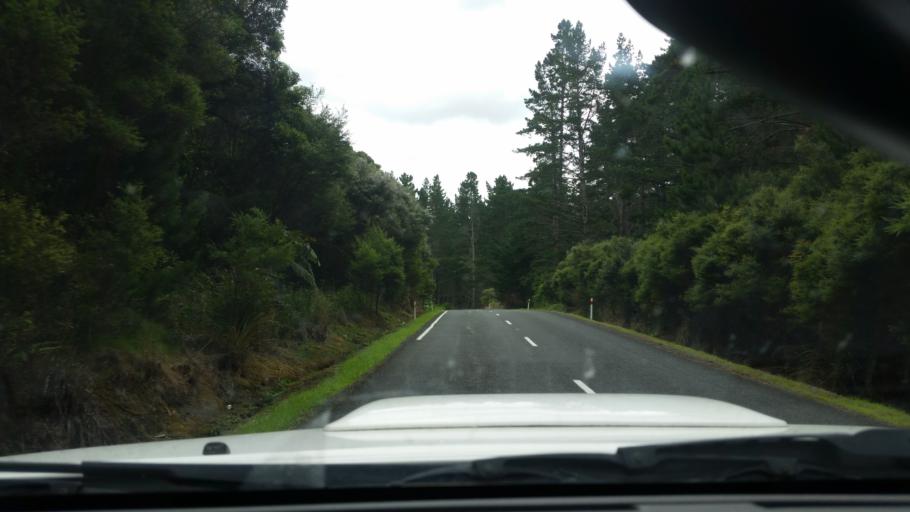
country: NZ
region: Northland
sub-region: Kaipara District
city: Dargaville
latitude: -35.7353
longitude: 173.8647
